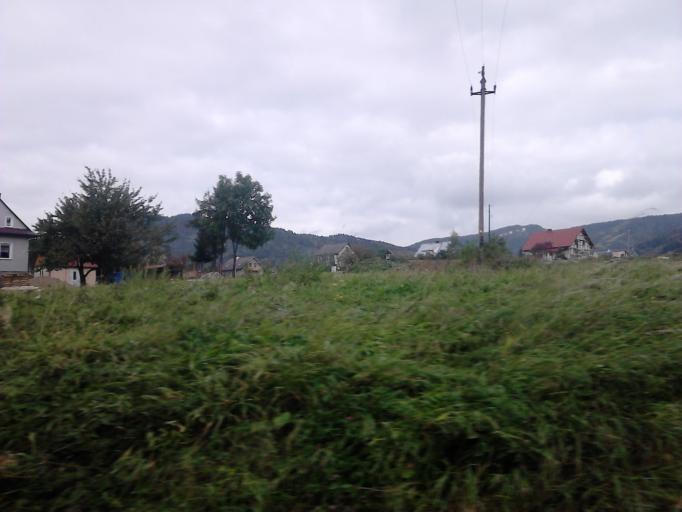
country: PL
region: Lesser Poland Voivodeship
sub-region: Powiat limanowski
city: Limanowa
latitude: 49.6997
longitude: 20.4606
